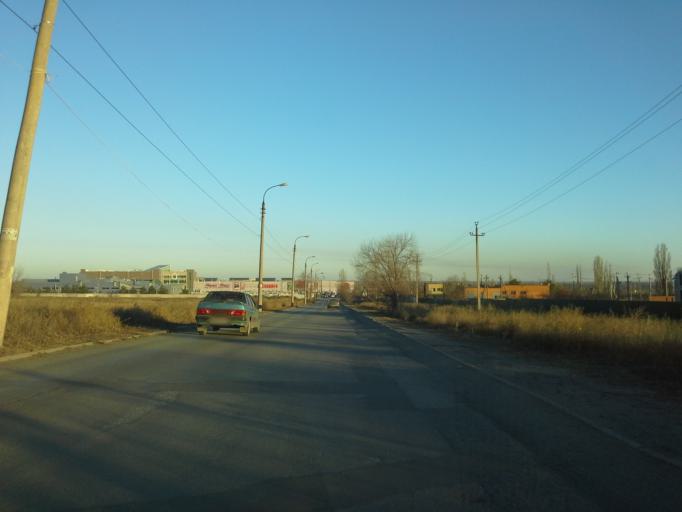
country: RU
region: Volgograd
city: Volgograd
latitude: 48.6371
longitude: 44.4247
